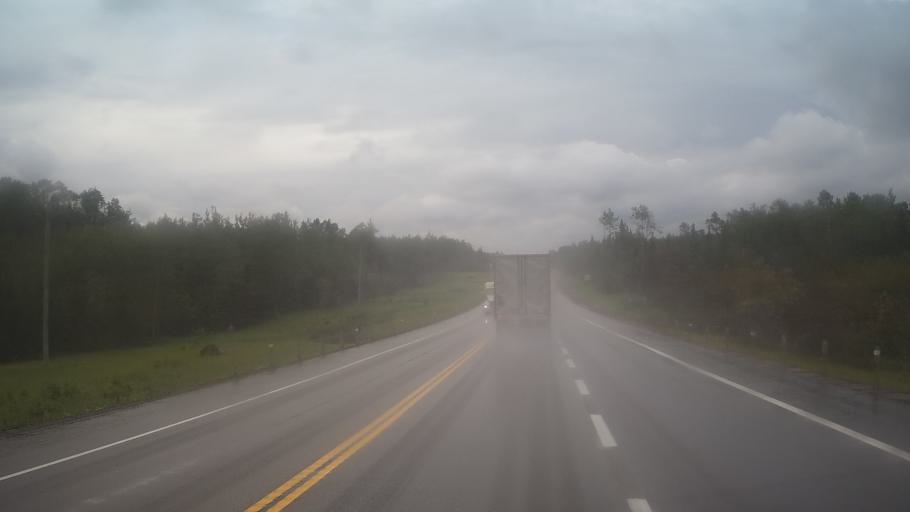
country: CA
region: Ontario
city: Neebing
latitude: 48.6291
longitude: -89.8959
